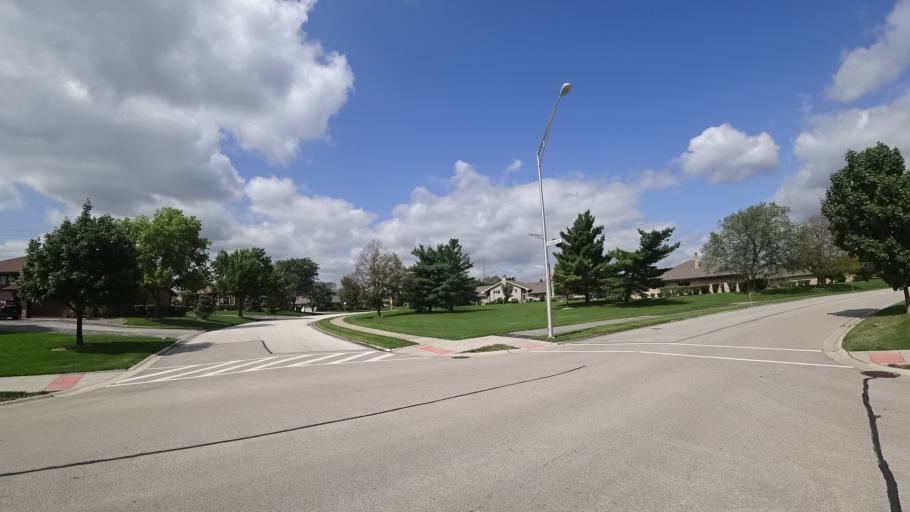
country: US
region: Illinois
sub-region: Will County
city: Mokena
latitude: 41.5613
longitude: -87.8811
